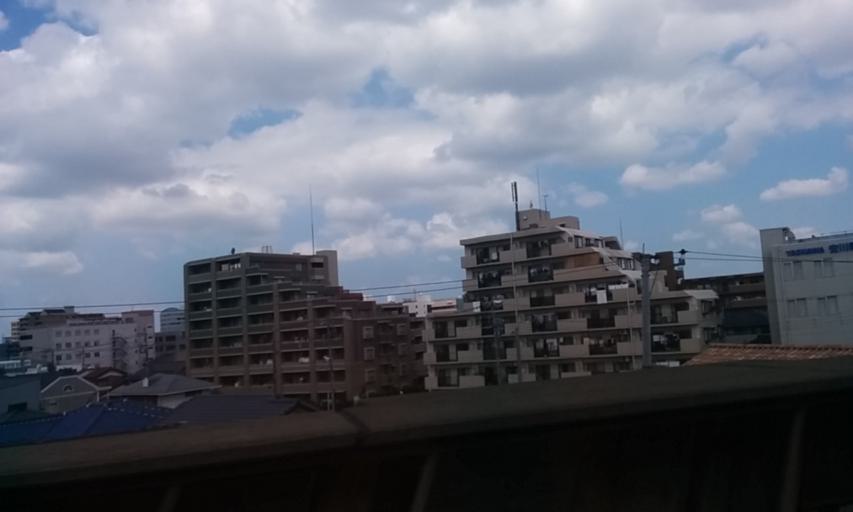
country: JP
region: Saitama
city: Ageoshimo
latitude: 35.9396
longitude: 139.6176
